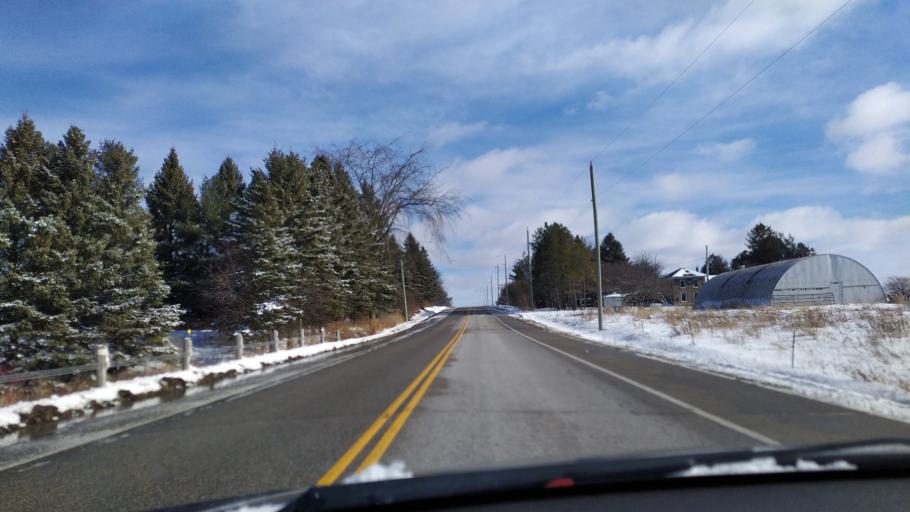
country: CA
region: Ontario
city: Waterloo
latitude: 43.4737
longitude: -80.7098
